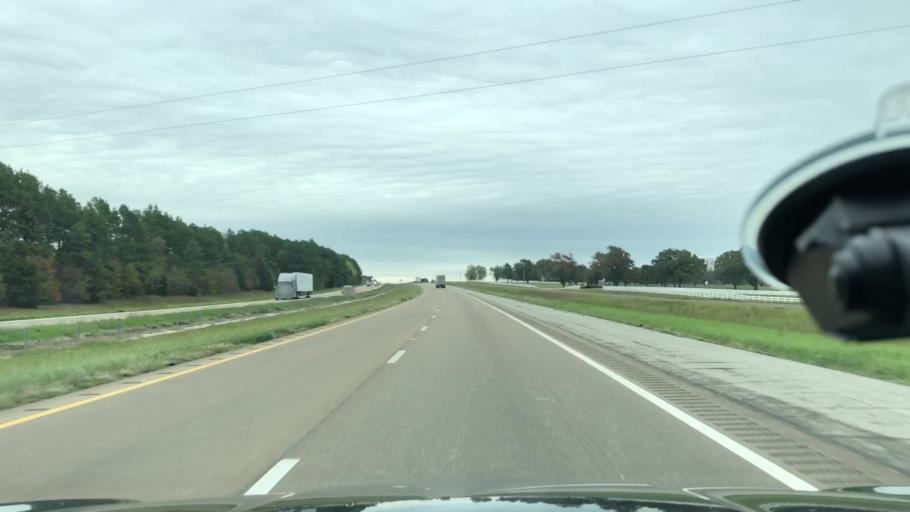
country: US
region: Texas
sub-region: Titus County
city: Mount Pleasant
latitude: 33.2041
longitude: -94.9092
